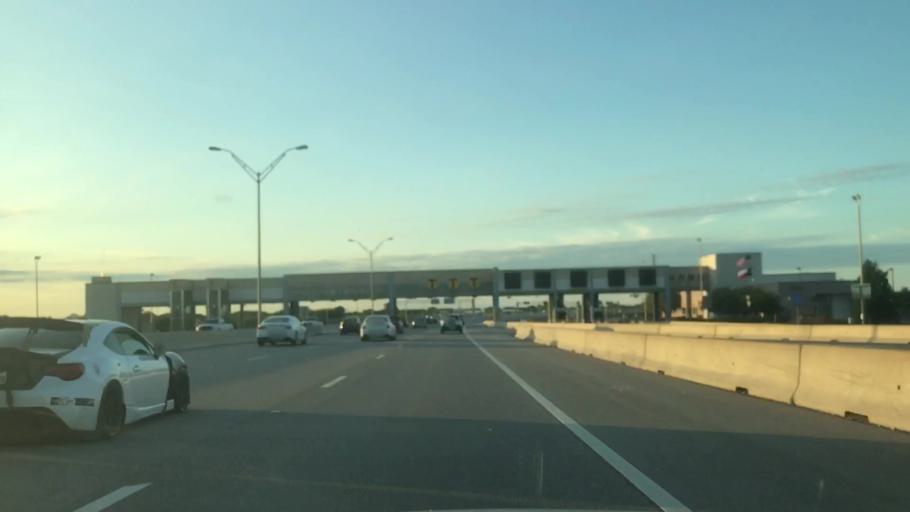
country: US
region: Texas
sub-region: Dallas County
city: Carrollton
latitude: 32.9581
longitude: -96.9284
